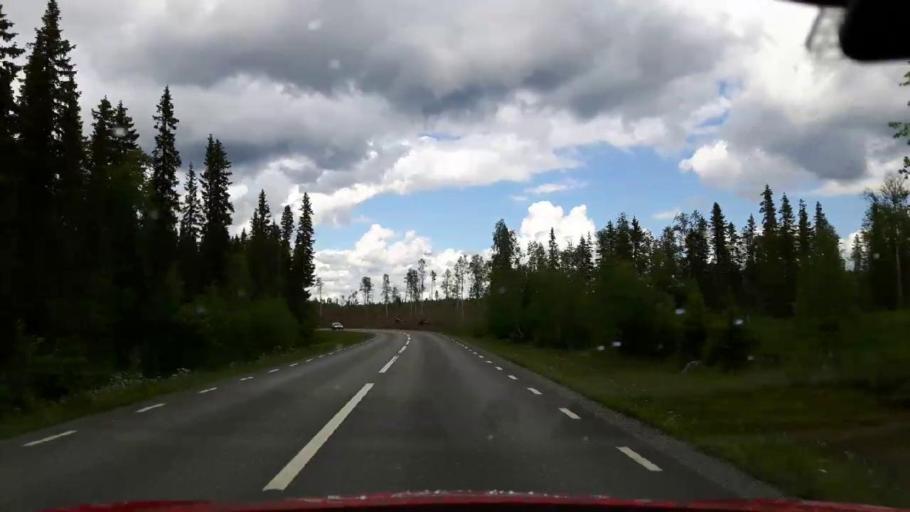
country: SE
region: Jaemtland
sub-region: Krokoms Kommun
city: Krokom
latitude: 63.7778
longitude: 14.3486
